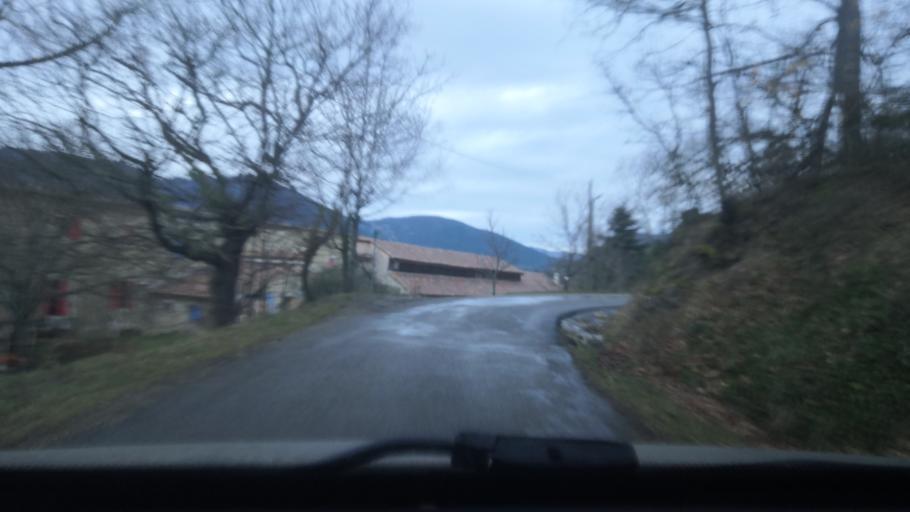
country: FR
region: Rhone-Alpes
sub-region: Departement de la Drome
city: Dieulefit
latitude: 44.5201
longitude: 5.0263
